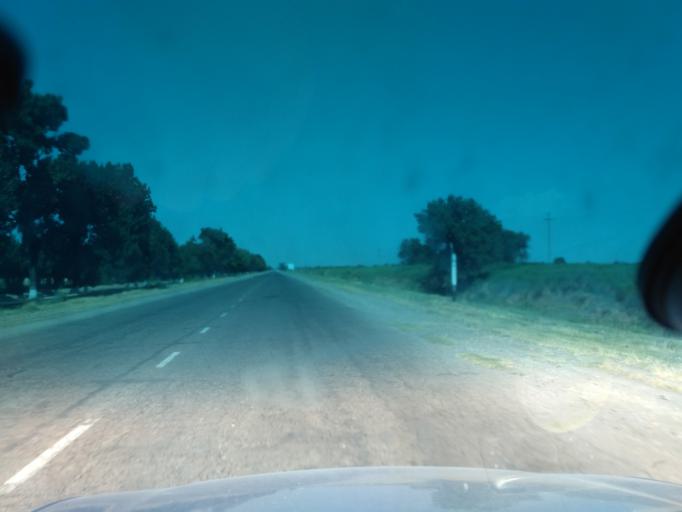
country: UZ
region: Sirdaryo
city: Guliston
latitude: 40.5037
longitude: 68.9561
